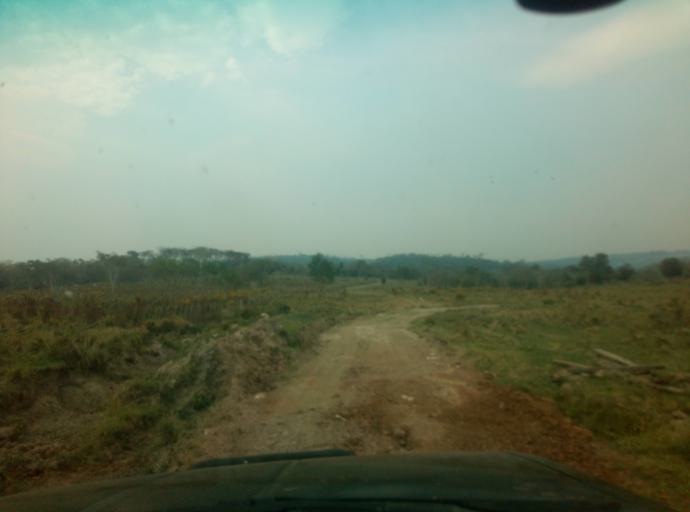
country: PY
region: Caaguazu
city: San Joaquin
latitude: -25.1020
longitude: -56.1241
